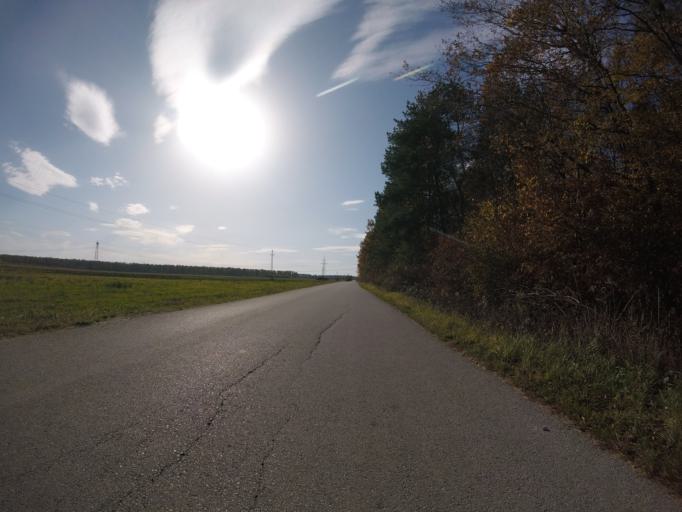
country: HR
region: Zagrebacka
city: Mraclin
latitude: 45.6526
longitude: 16.0706
